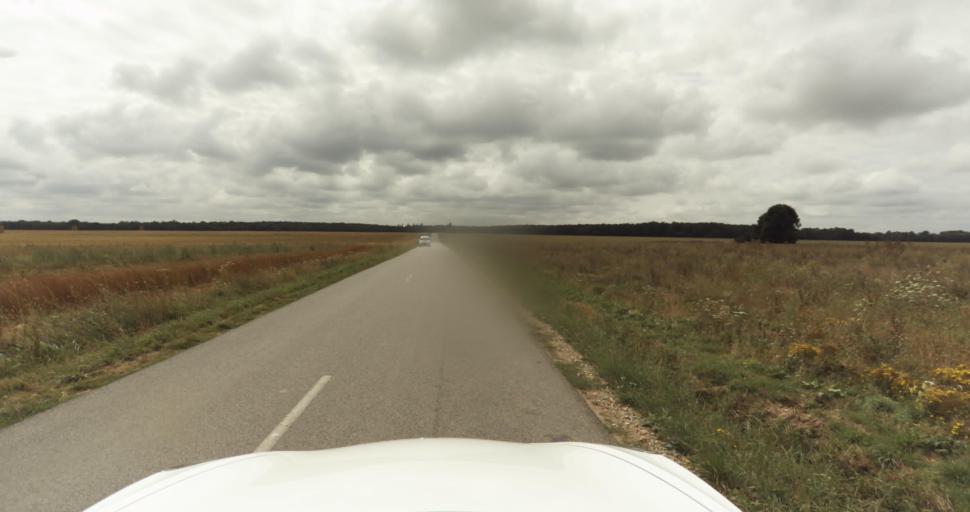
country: FR
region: Haute-Normandie
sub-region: Departement de l'Eure
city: Claville
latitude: 49.0146
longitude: 1.0340
